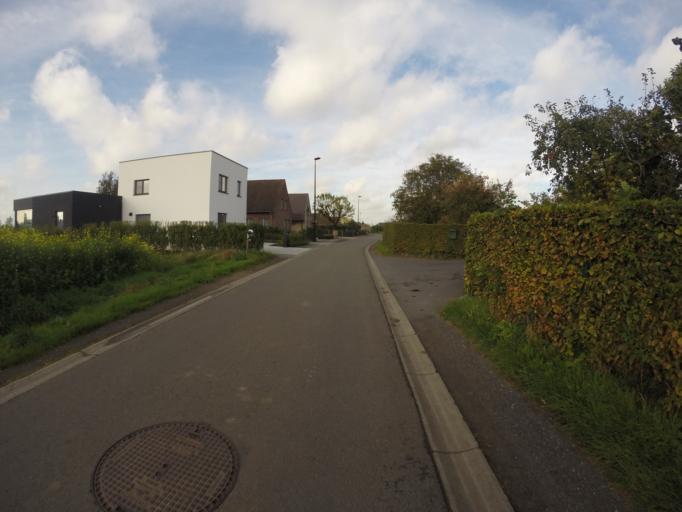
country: BE
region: Flanders
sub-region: Provincie Oost-Vlaanderen
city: Knesselare
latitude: 51.1268
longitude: 3.4106
